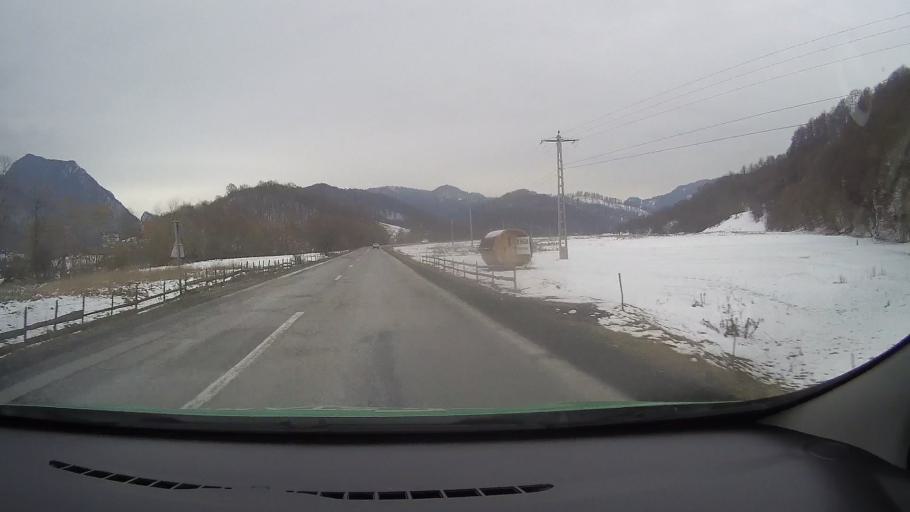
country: RO
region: Brasov
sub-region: Oras Rasnov
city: Rasnov
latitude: 45.5488
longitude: 25.4943
